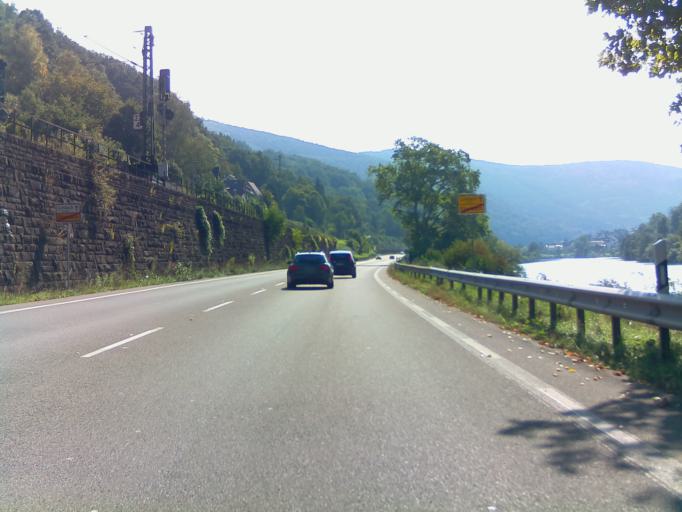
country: DE
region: Baden-Wuerttemberg
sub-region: Karlsruhe Region
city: Eberbach
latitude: 49.4572
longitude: 8.9910
